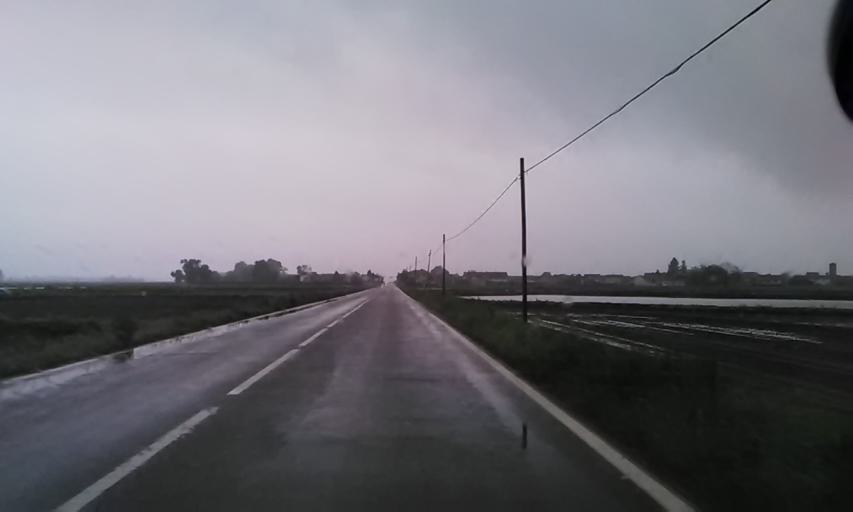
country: IT
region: Piedmont
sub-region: Provincia di Vercelli
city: Oldenico
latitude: 45.3969
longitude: 8.3793
